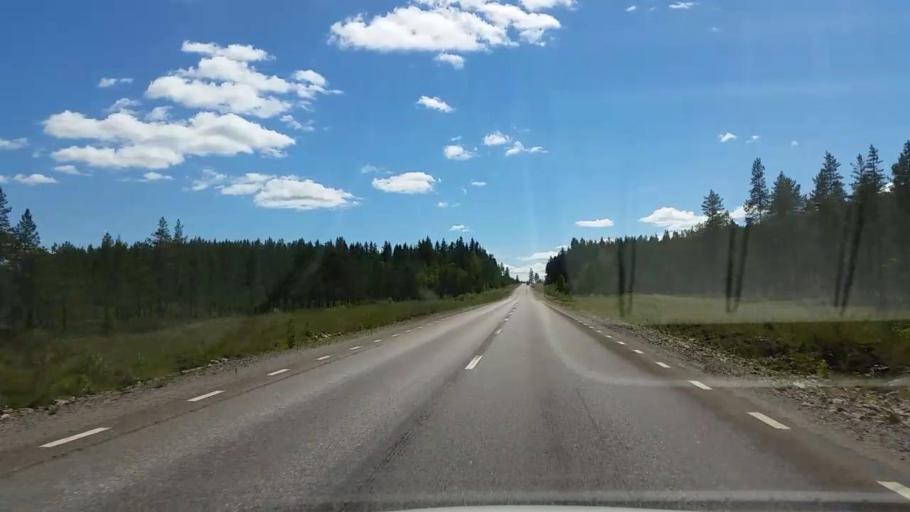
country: SE
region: Gaevleborg
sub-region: Bollnas Kommun
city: Vittsjo
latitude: 61.1154
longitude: 15.8638
